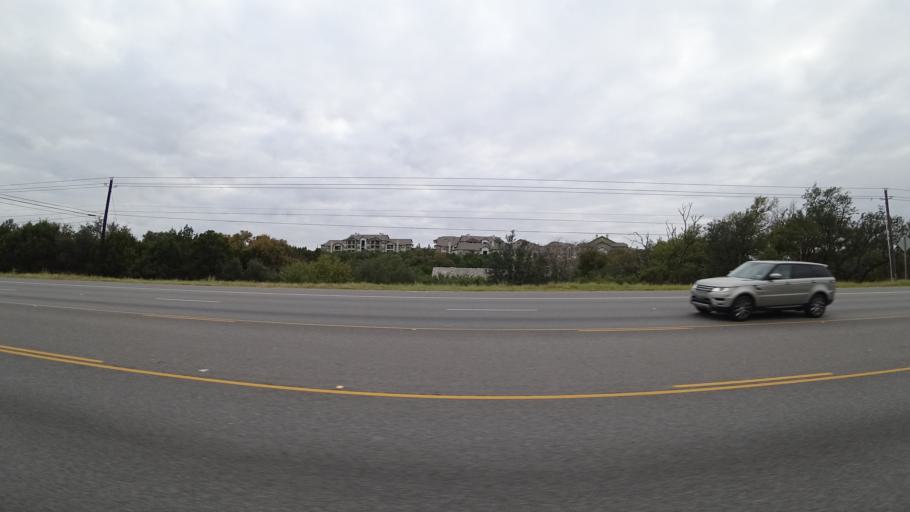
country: US
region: Texas
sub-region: Travis County
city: Bee Cave
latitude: 30.3216
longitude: -97.9552
